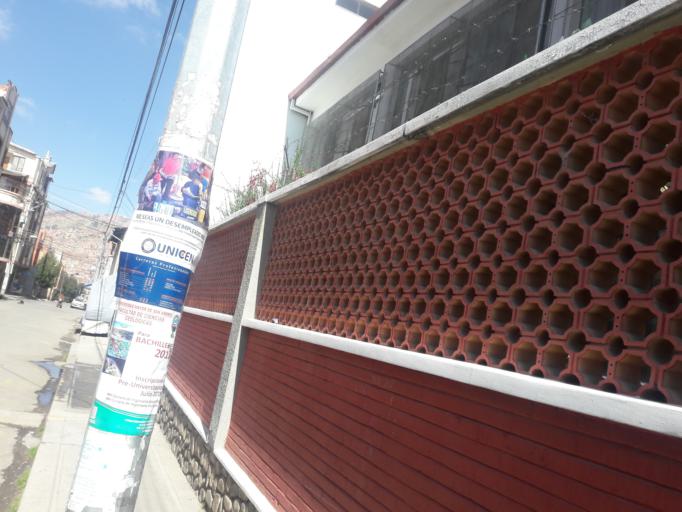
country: BO
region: La Paz
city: La Paz
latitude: -16.4905
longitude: -68.1490
